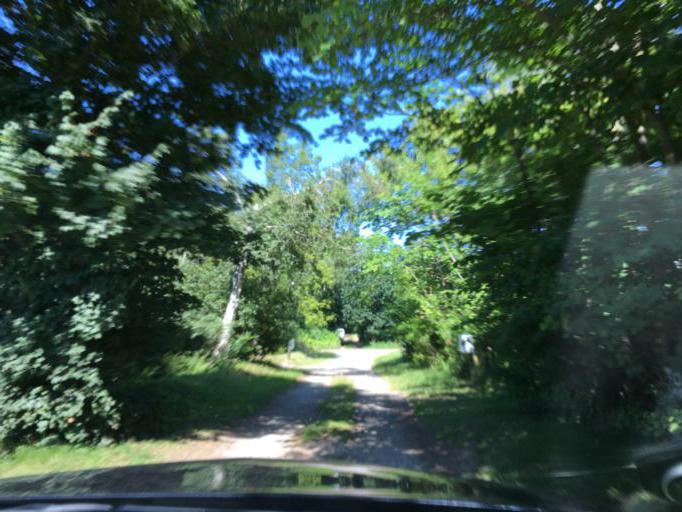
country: DK
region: Capital Region
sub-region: Gribskov Kommune
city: Helsinge
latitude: 56.0947
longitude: 12.1640
